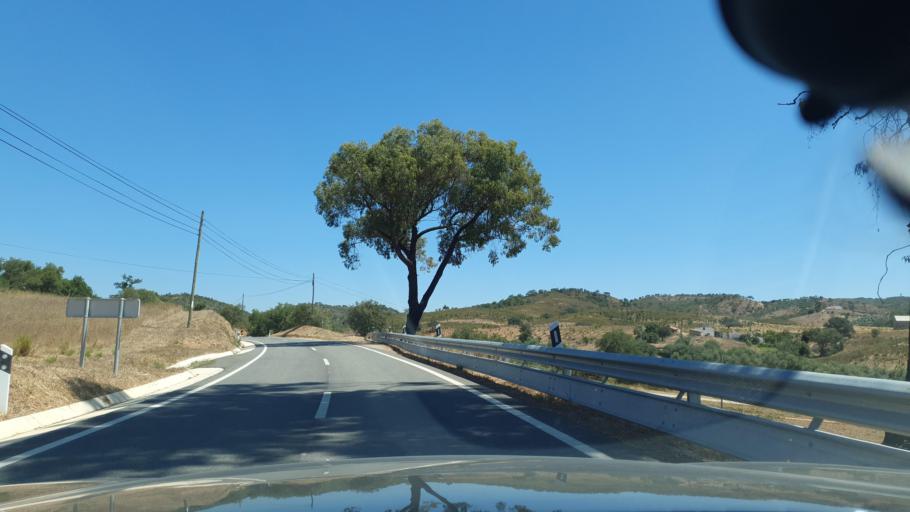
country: PT
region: Beja
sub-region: Odemira
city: Odemira
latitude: 37.5155
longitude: -8.4757
